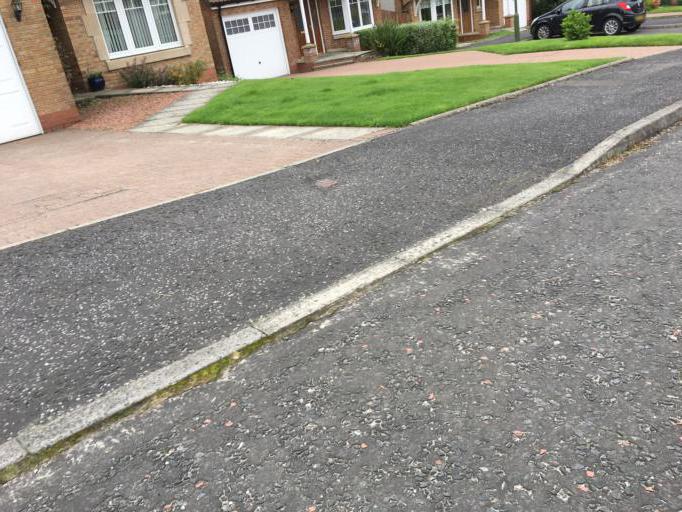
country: GB
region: Scotland
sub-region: West Lothian
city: Mid Calder
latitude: 55.8692
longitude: -3.5056
